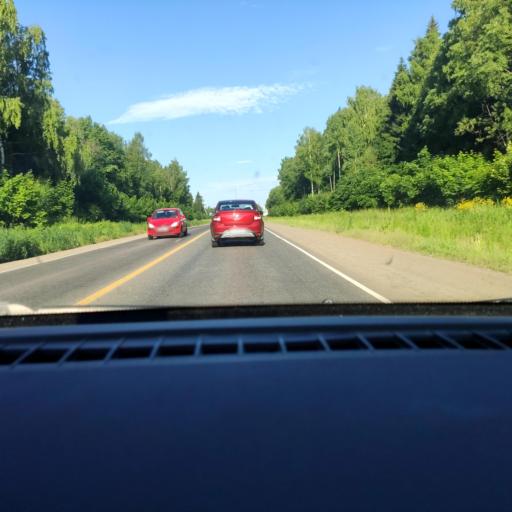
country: RU
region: Udmurtiya
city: Khokhryaki
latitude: 56.9156
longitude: 53.4258
